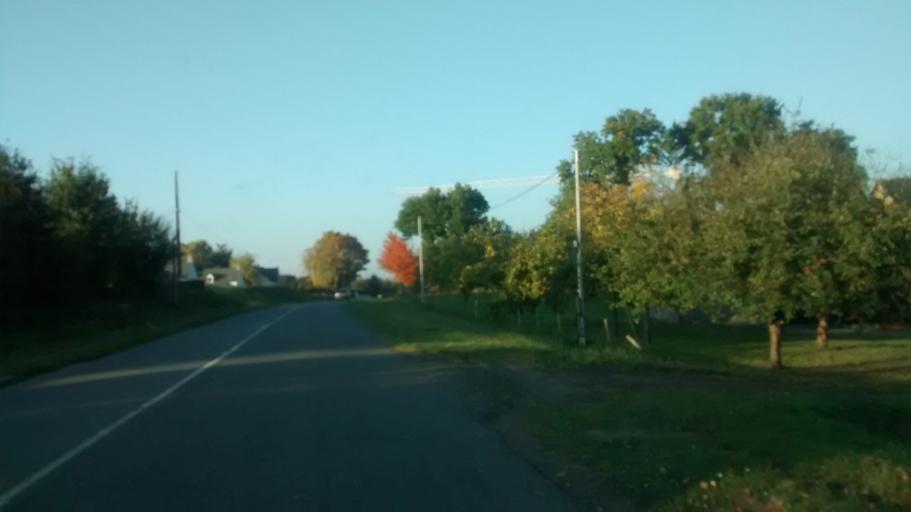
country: FR
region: Brittany
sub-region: Departement d'Ille-et-Vilaine
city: Le Rheu
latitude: 48.1265
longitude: -1.8054
